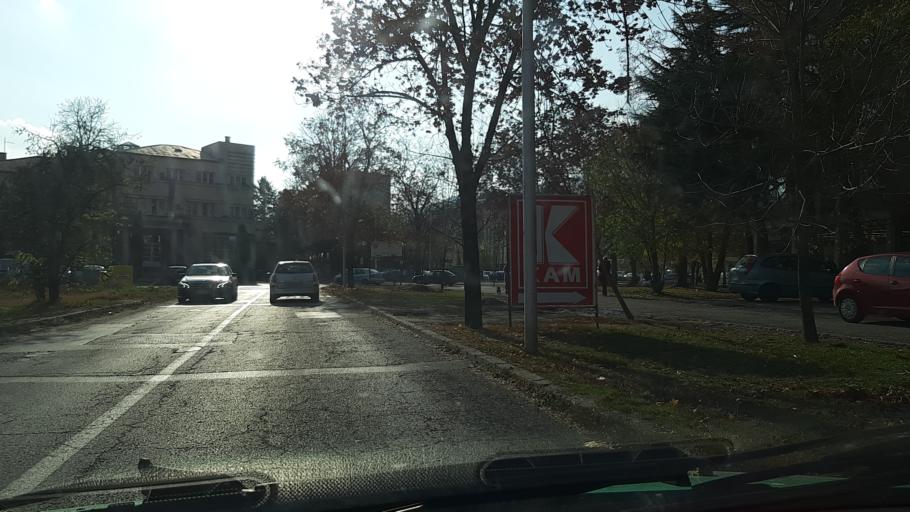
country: MK
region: Kisela Voda
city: Usje
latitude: 41.9846
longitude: 21.4594
